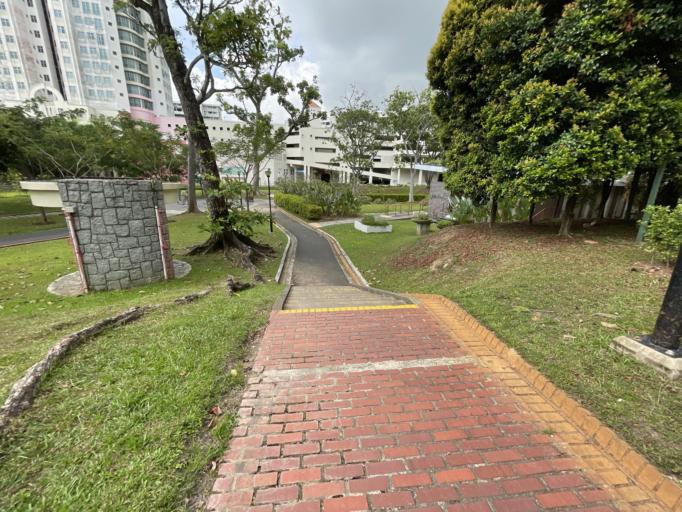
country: SG
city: Singapore
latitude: 1.3028
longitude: 103.7667
